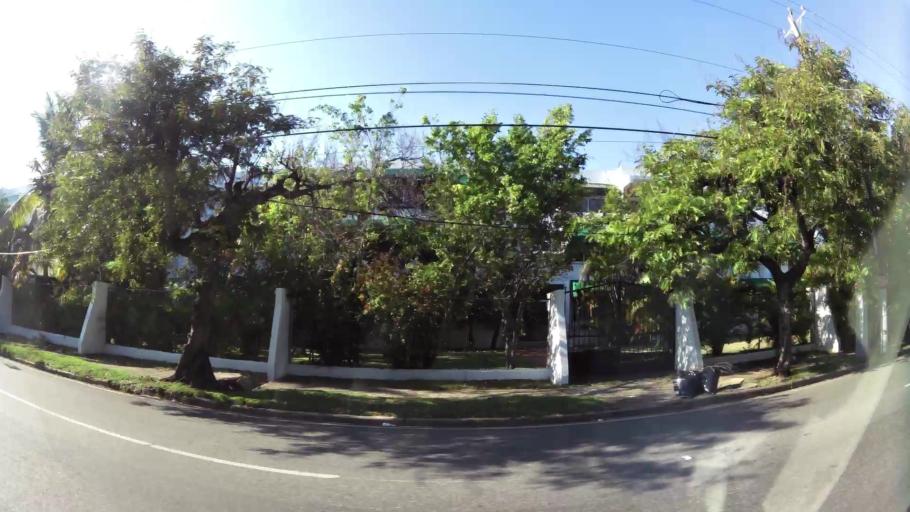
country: DO
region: Nacional
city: Bella Vista
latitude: 18.4437
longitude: -69.9555
